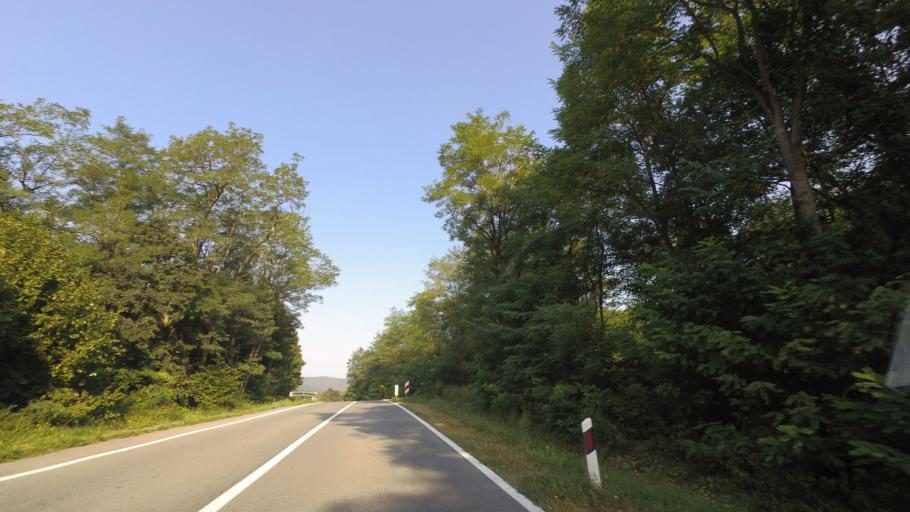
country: HR
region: Pozesko-Slavonska
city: Velika
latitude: 45.4361
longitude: 17.4960
